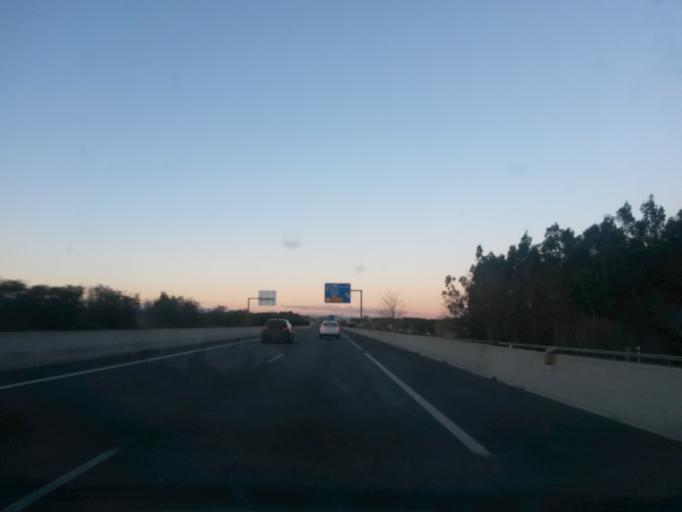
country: ES
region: Catalonia
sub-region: Provincia de Girona
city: Riudellots de la Selva
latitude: 41.8787
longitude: 2.7803
